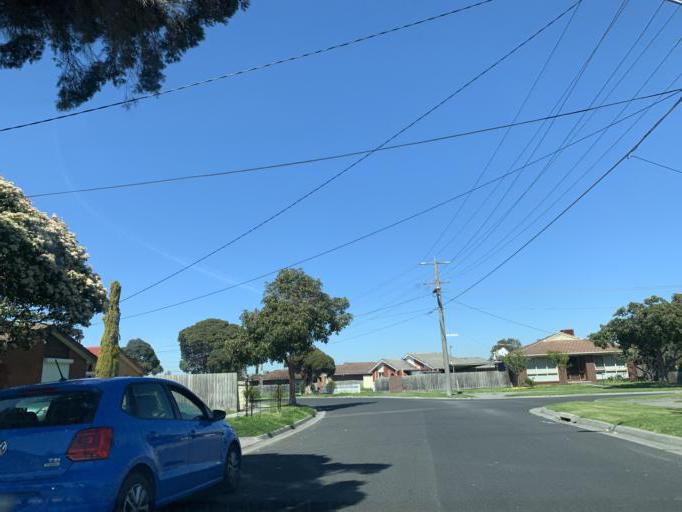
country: AU
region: Victoria
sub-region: Greater Dandenong
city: Dandenong
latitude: -37.9984
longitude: 145.2021
